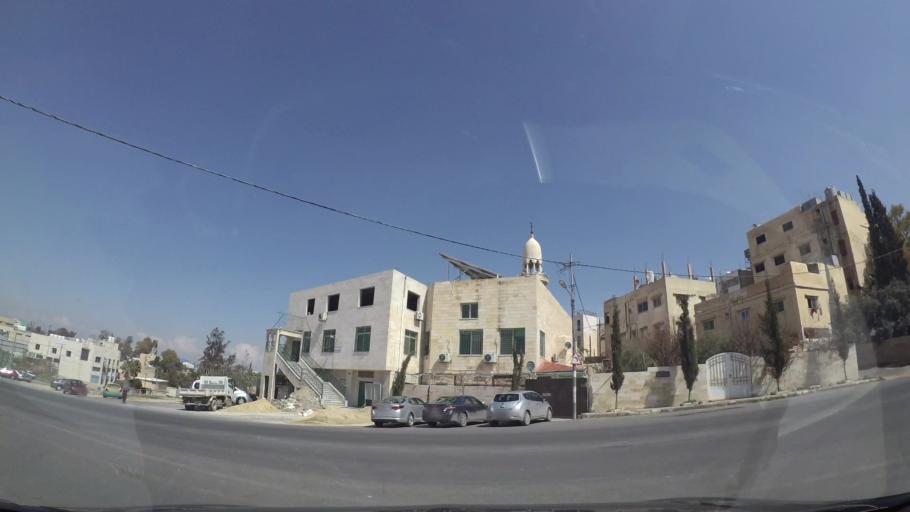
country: JO
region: Zarqa
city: Russeifa
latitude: 31.9888
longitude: 36.0156
